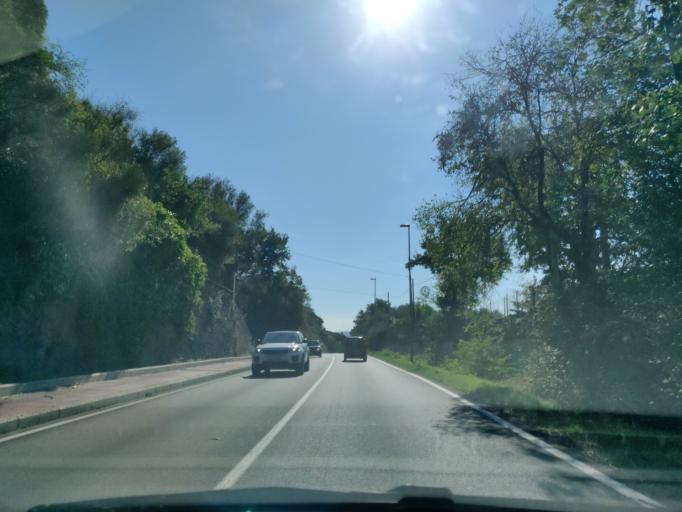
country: IT
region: Latium
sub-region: Provincia di Viterbo
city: Viterbo
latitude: 42.4179
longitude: 12.0877
